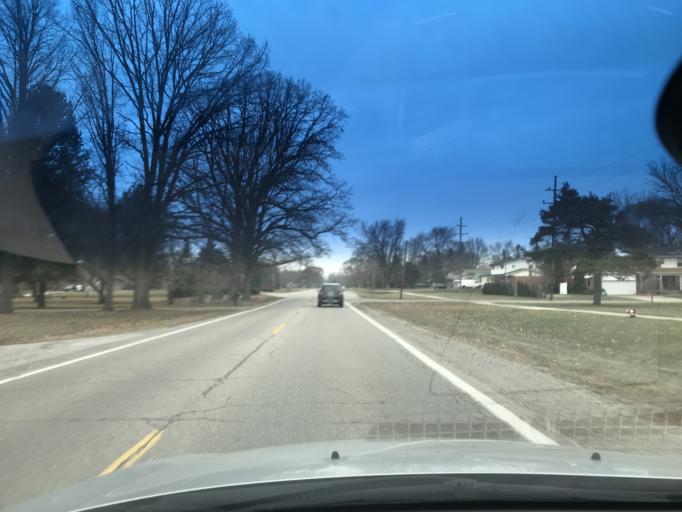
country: US
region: Michigan
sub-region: Macomb County
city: Shelby
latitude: 42.6736
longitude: -83.0537
